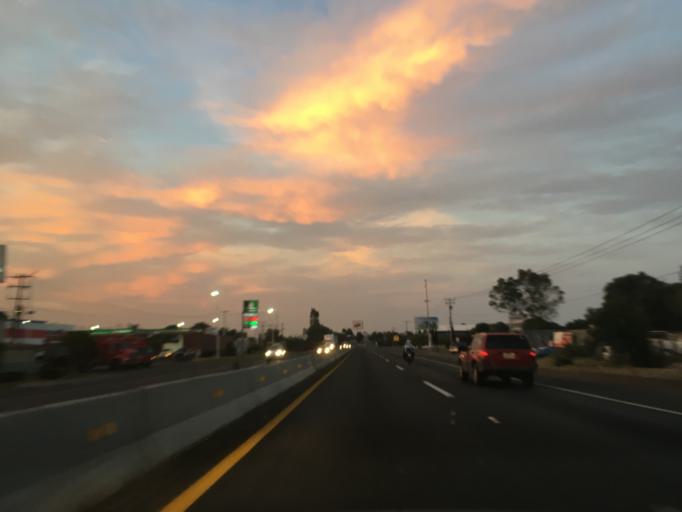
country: MX
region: Michoacan
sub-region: Morelia
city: Morelos
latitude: 19.6538
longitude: -101.2441
